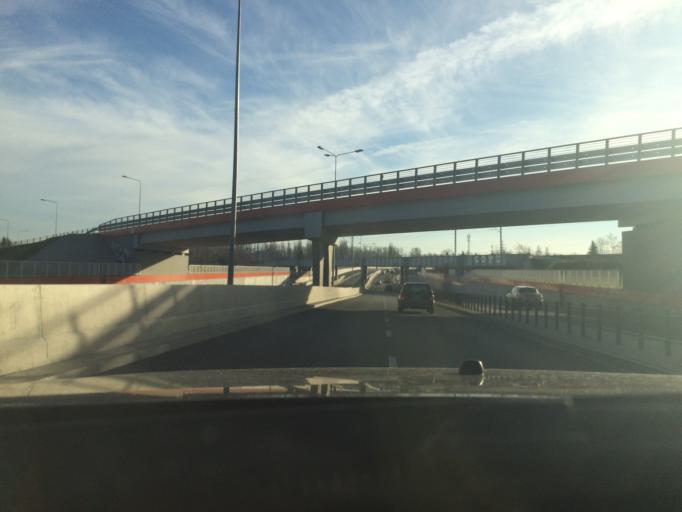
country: PL
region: Lodz Voivodeship
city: Lodz
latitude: 51.7238
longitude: 19.4515
